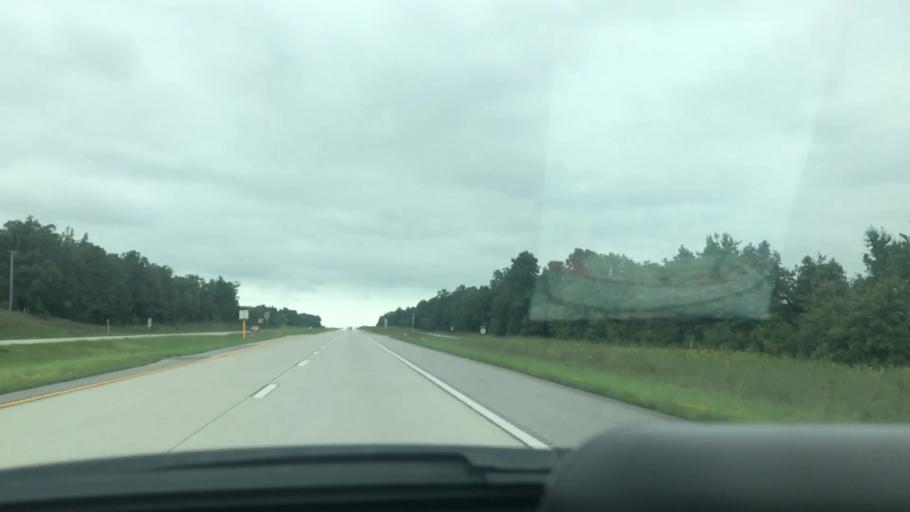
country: US
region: Missouri
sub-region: Greene County
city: Fair Grove
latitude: 37.4731
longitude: -93.1394
